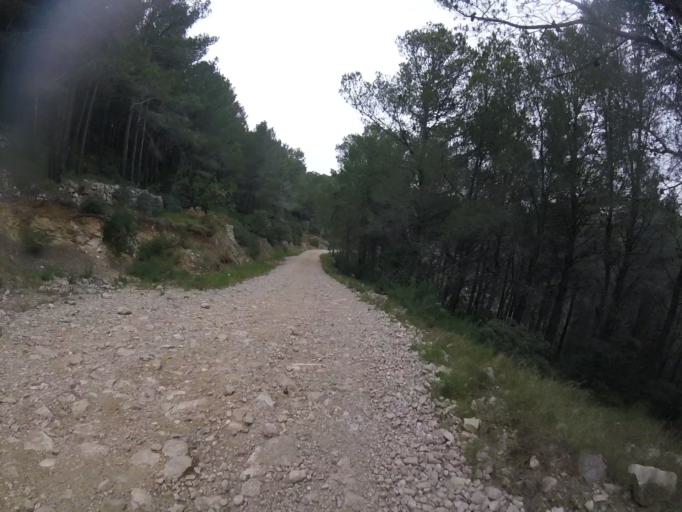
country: ES
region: Valencia
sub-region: Provincia de Castello
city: Alcala de Xivert
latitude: 40.3111
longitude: 0.2637
